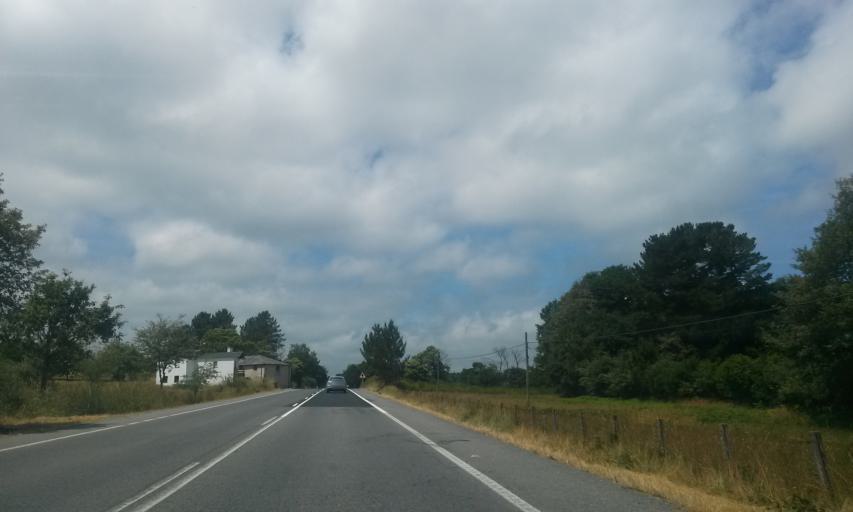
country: ES
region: Galicia
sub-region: Provincia de Lugo
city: Friol
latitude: 43.0335
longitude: -7.7318
